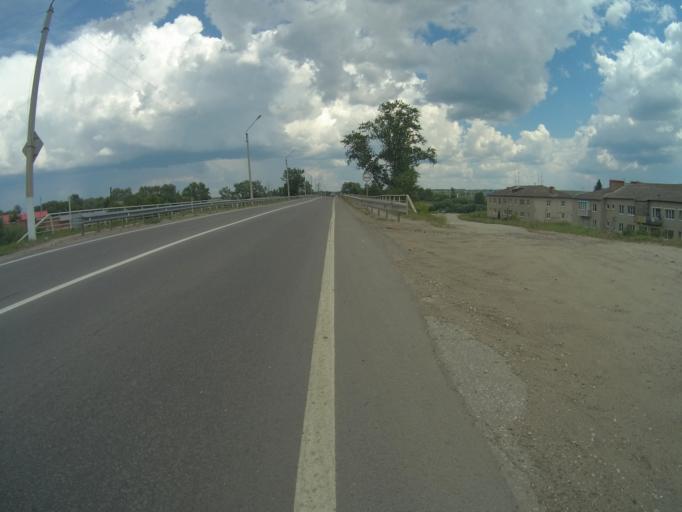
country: RU
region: Vladimir
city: Bogolyubovo
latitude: 56.1998
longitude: 40.5468
